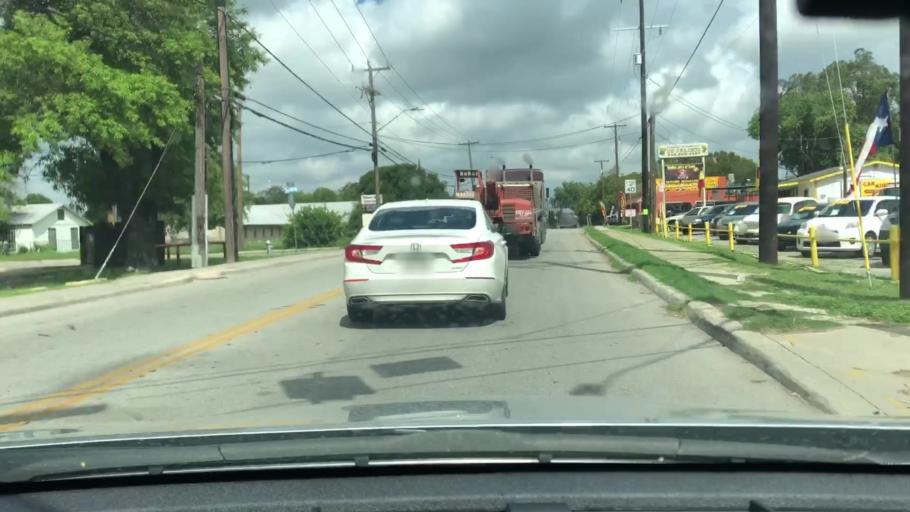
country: US
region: Texas
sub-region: Bexar County
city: Windcrest
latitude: 29.5333
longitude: -98.3792
